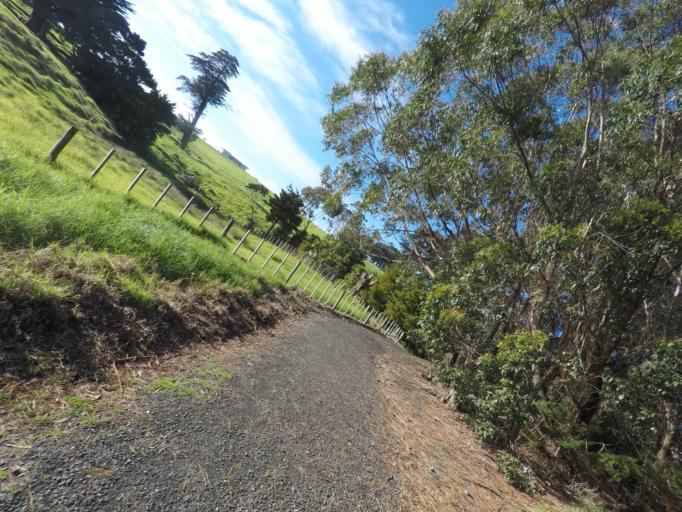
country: NZ
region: Auckland
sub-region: Auckland
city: Warkworth
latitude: -36.4300
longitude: 174.7185
